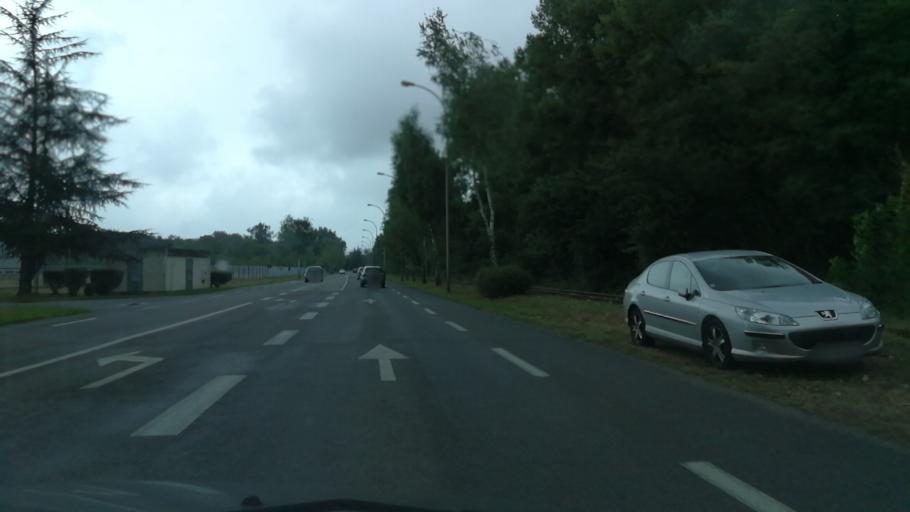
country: FR
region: Aquitaine
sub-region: Departement des Pyrenees-Atlantiques
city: Mourenx
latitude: 43.3864
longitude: -0.5841
